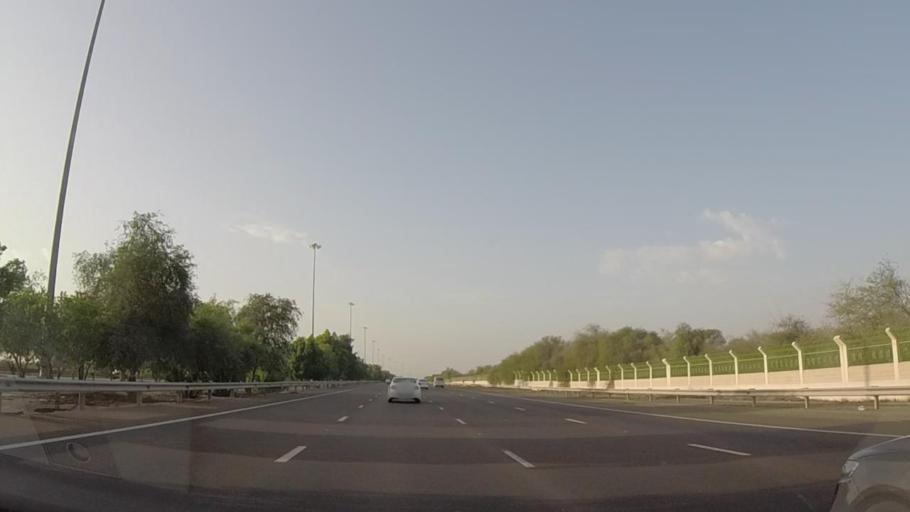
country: AE
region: Dubai
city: Dubai
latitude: 24.7754
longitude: 54.8516
